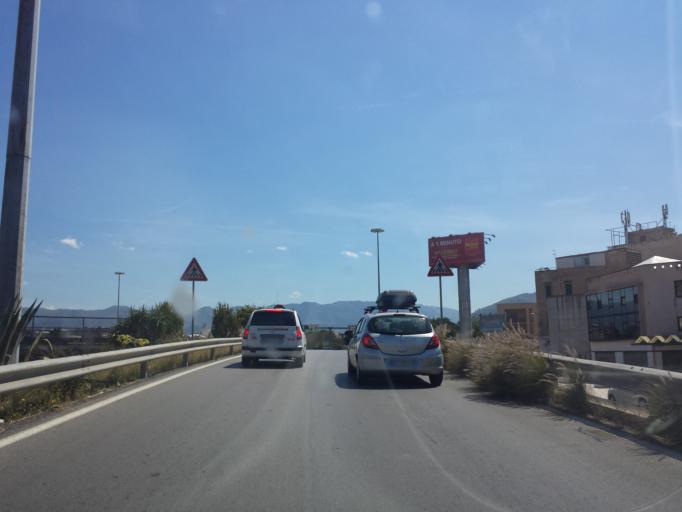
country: IT
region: Sicily
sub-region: Palermo
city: Palermo
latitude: 38.1412
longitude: 13.3311
